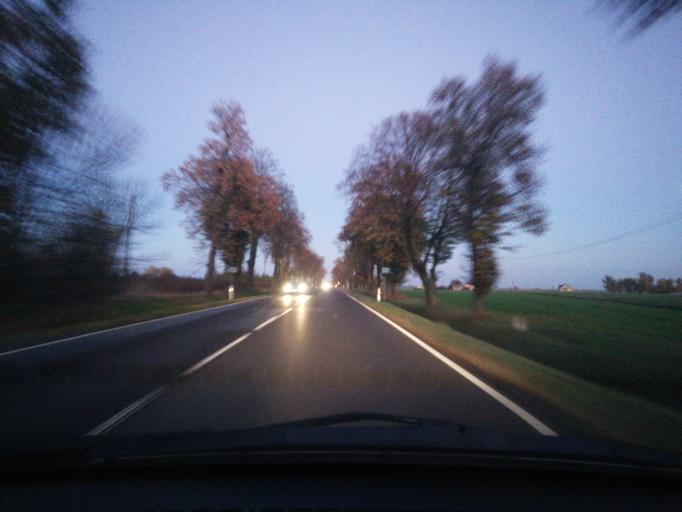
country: PL
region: Lodz Voivodeship
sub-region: Powiat brzezinski
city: Rogow
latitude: 51.8093
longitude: 19.9198
